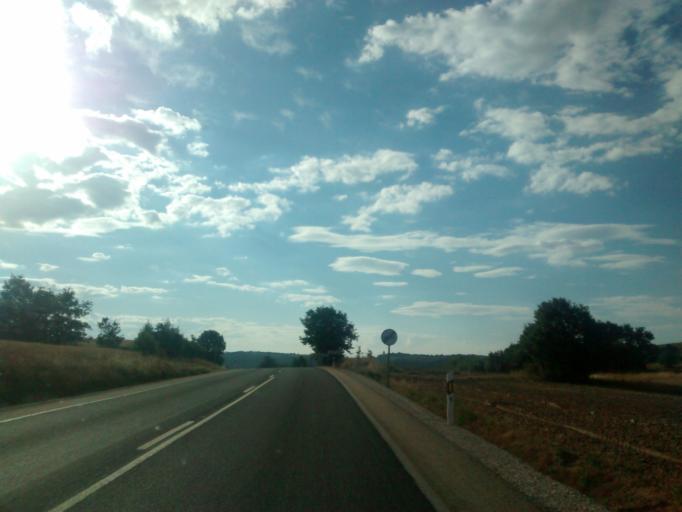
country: ES
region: Castille and Leon
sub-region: Provincia de Burgos
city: Basconcillos del Tozo
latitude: 42.6712
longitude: -3.9298
